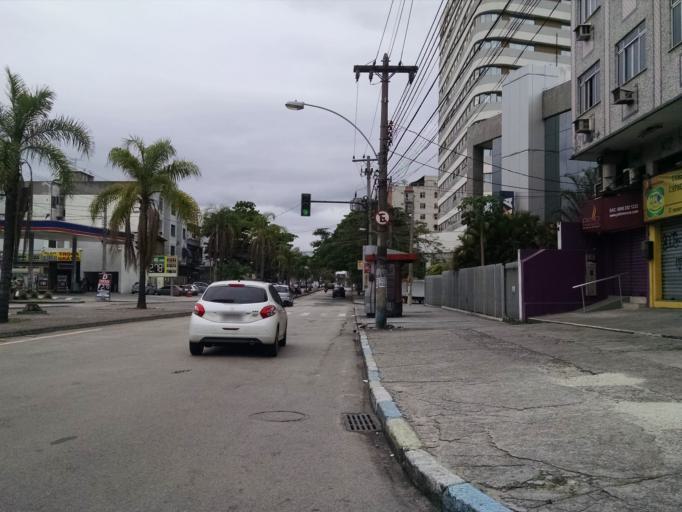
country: BR
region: Rio de Janeiro
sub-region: Duque De Caxias
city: Duque de Caxias
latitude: -22.8399
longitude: -43.3128
